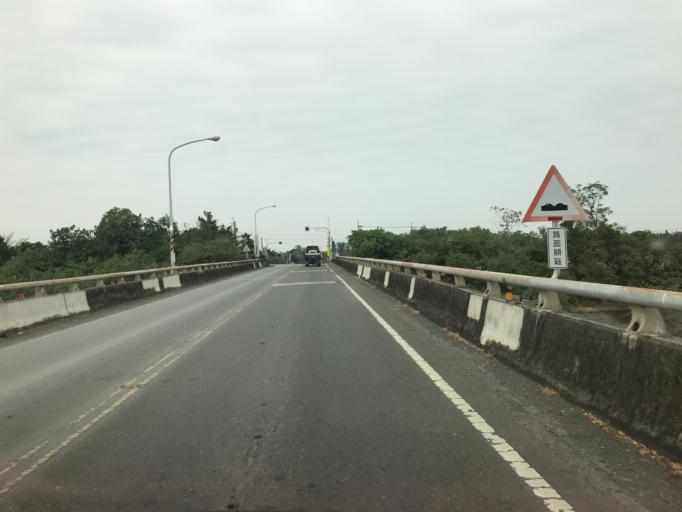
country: TW
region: Taiwan
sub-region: Pingtung
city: Pingtung
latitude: 22.4936
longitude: 120.5928
